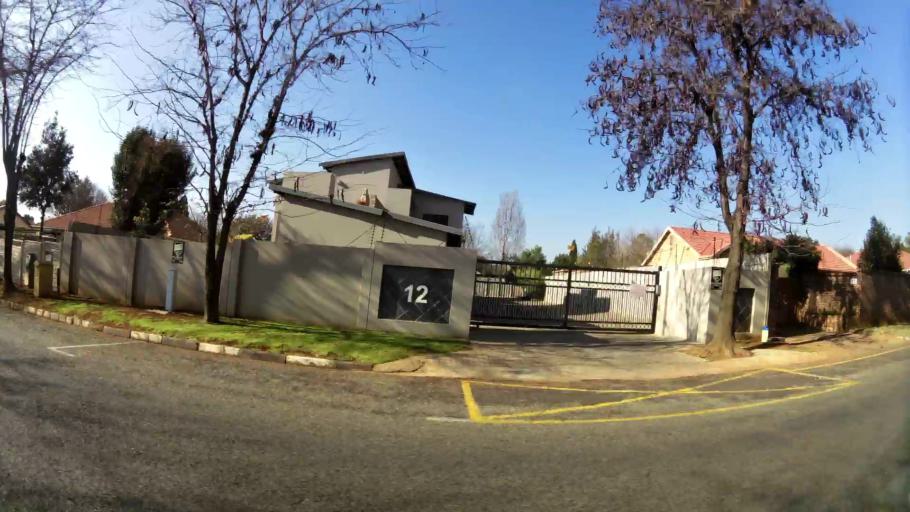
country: ZA
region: Gauteng
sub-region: City of Johannesburg Metropolitan Municipality
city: Modderfontein
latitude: -26.1484
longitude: 28.1604
